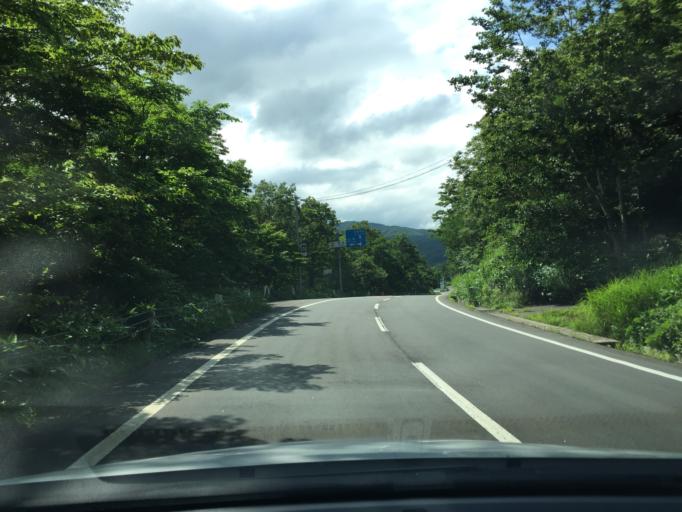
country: JP
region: Fukushima
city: Inawashiro
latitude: 37.2713
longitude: 140.0785
